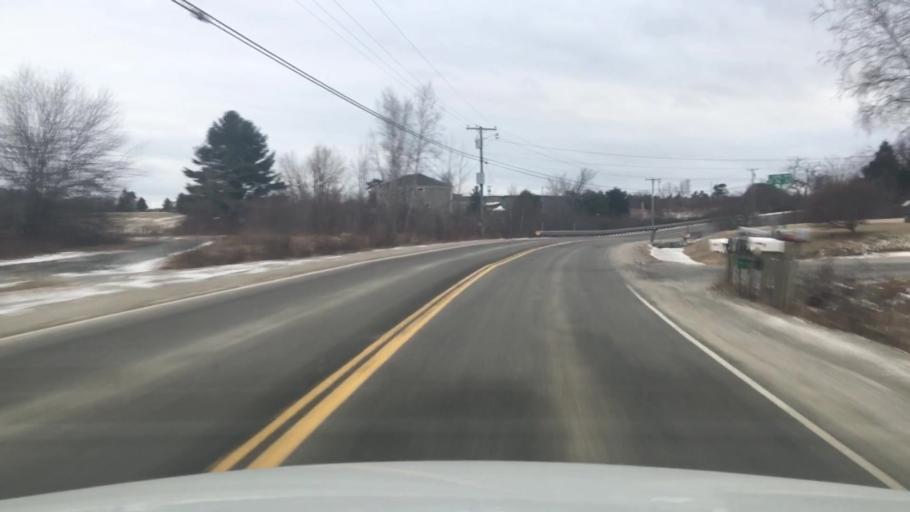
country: US
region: Maine
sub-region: Hancock County
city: Trenton
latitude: 44.4912
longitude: -68.3634
